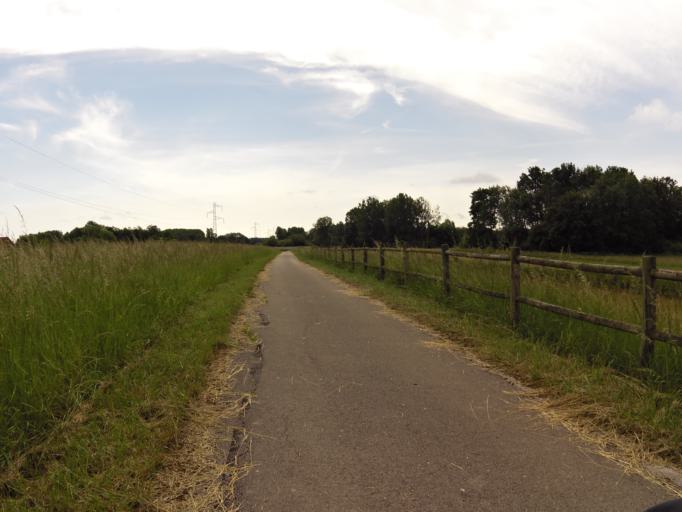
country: FR
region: Champagne-Ardenne
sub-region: Departement de l'Aube
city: Lusigny-sur-Barse
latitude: 48.2707
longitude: 4.2424
